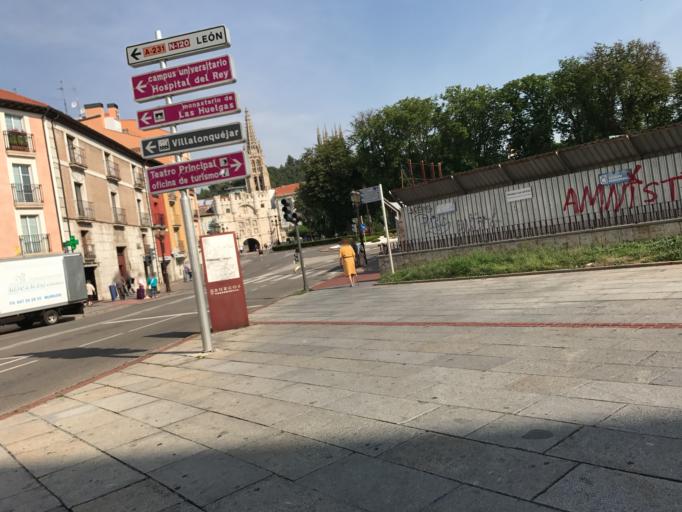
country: ES
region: Castille and Leon
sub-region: Provincia de Burgos
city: Burgos
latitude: 42.3385
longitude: -3.7021
